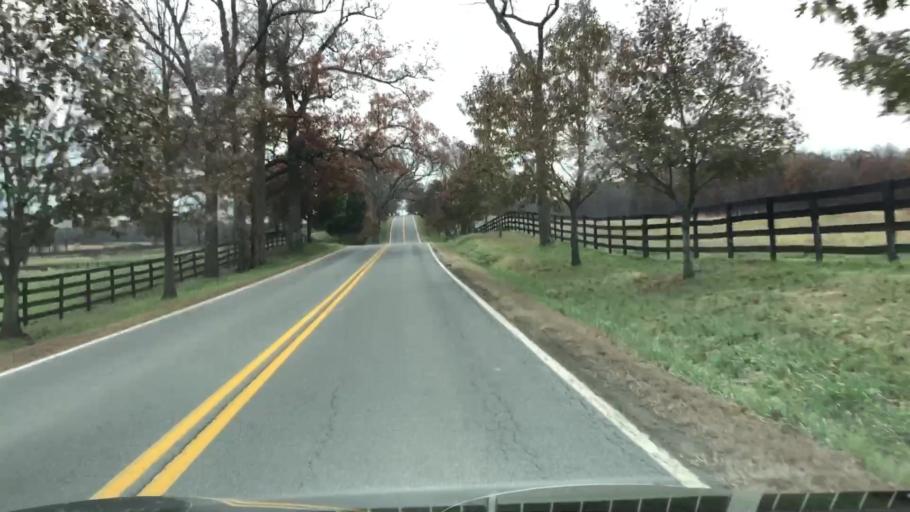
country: US
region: Virginia
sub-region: Fauquier County
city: New Baltimore
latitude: 38.7708
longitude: -77.6813
